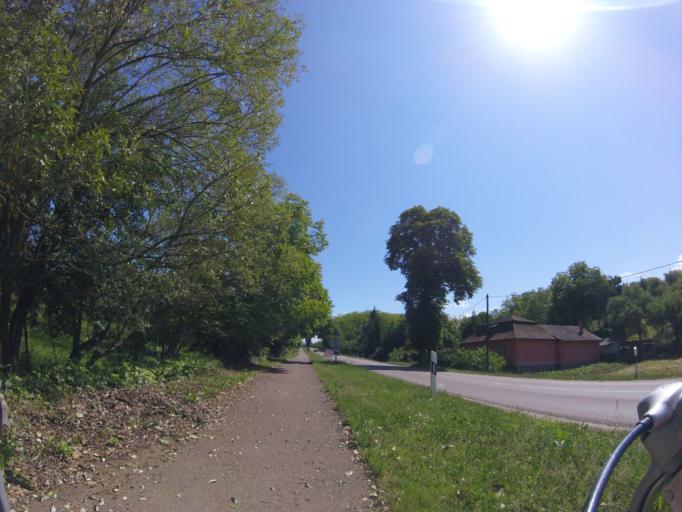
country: HU
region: Heves
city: Matraderecske
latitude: 47.9266
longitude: 20.0900
